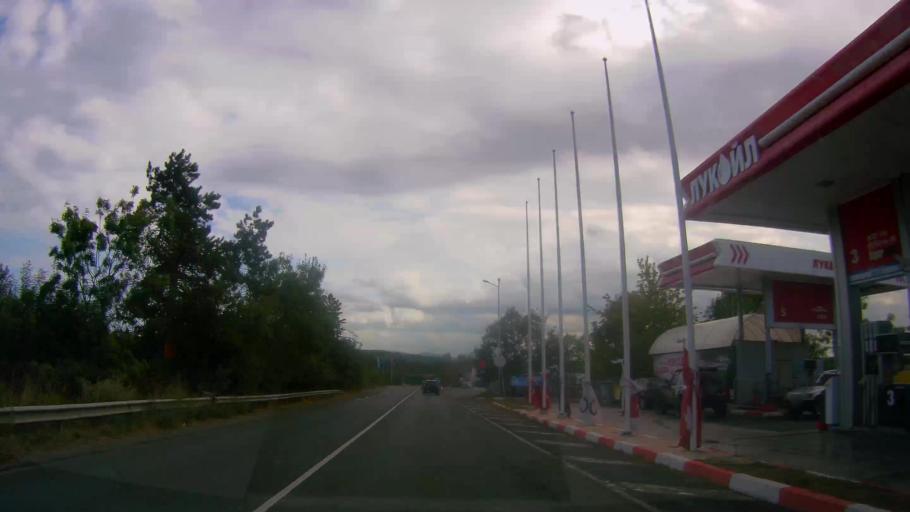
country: BG
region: Burgas
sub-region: Obshtina Primorsko
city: Primorsko
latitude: 42.2684
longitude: 27.7425
